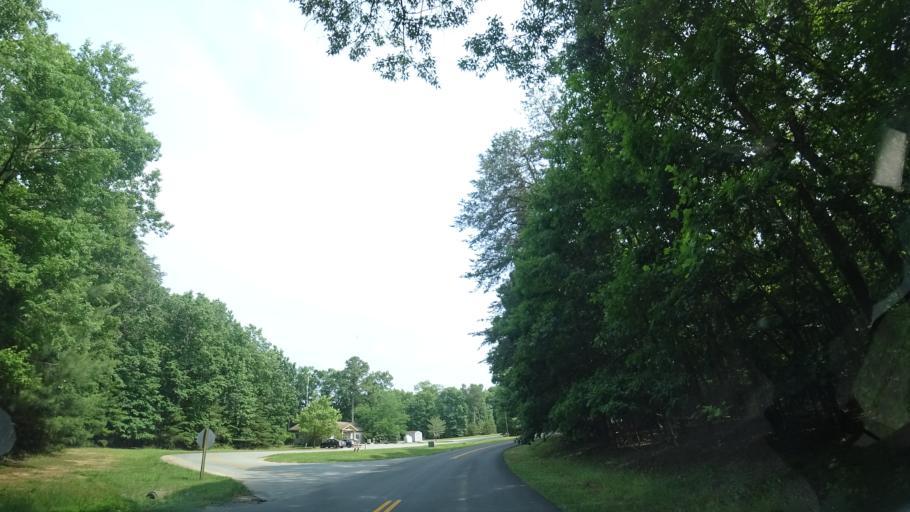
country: US
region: Virginia
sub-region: Louisa County
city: Louisa
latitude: 38.1204
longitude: -77.8231
